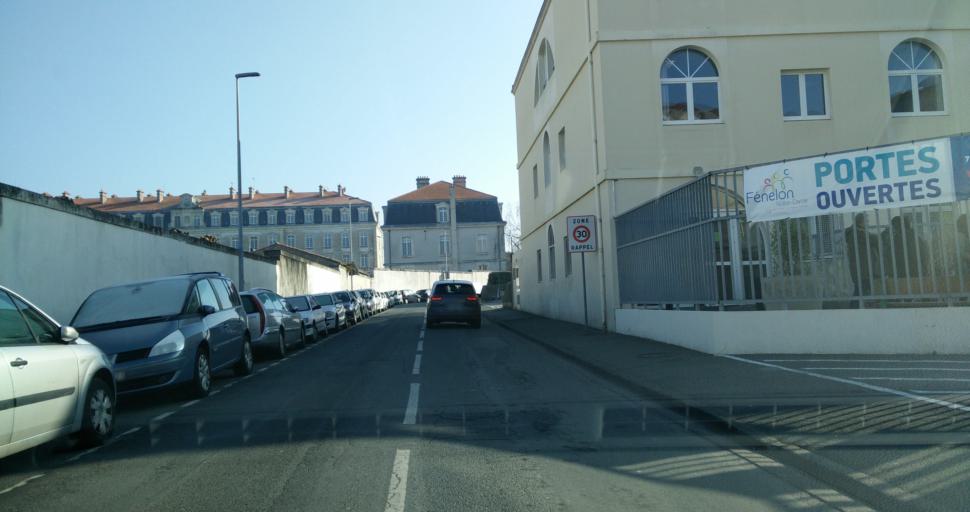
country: FR
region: Poitou-Charentes
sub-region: Departement de la Charente-Maritime
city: La Rochelle
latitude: 46.1666
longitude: -1.1500
